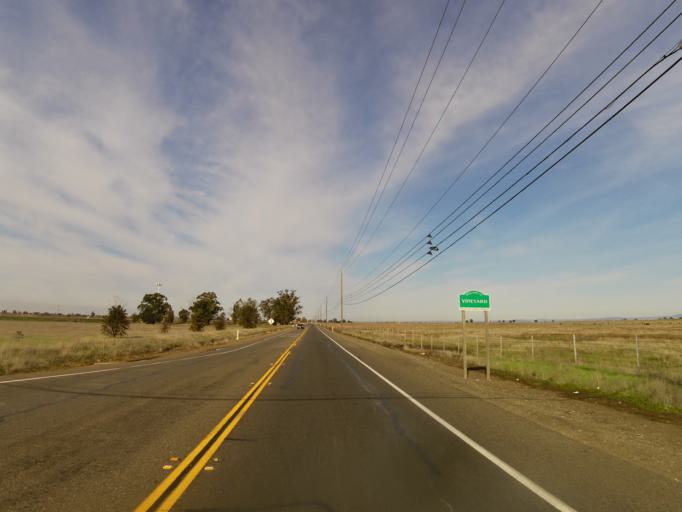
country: US
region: California
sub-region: Sacramento County
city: Wilton
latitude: 38.4856
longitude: -121.2422
